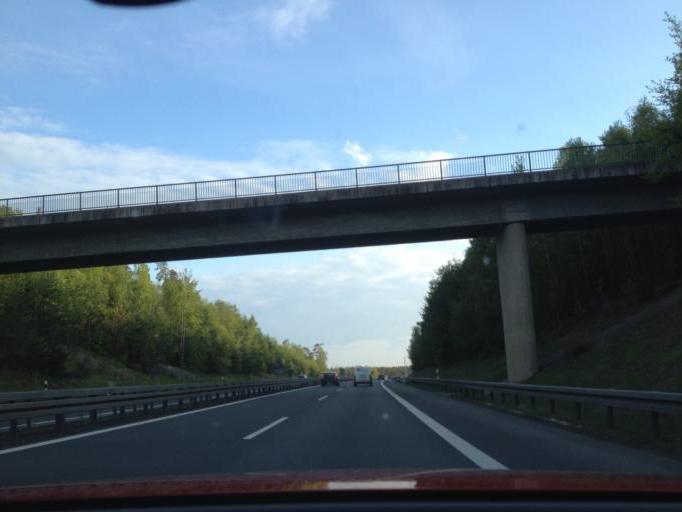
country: DE
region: Bavaria
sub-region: Upper Palatinate
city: Wiesau
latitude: 49.8954
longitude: 12.2195
